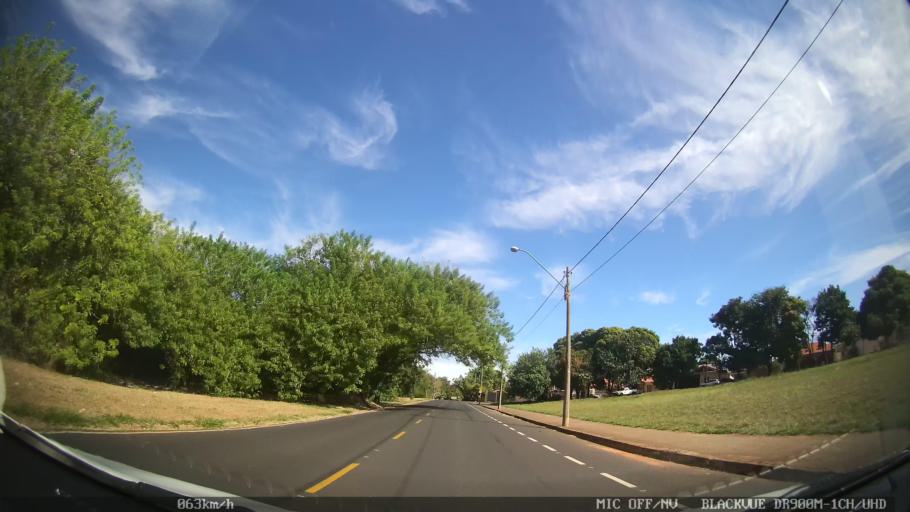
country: BR
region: Sao Paulo
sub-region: Sao Jose Do Rio Preto
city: Sao Jose do Rio Preto
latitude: -20.8495
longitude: -49.3636
